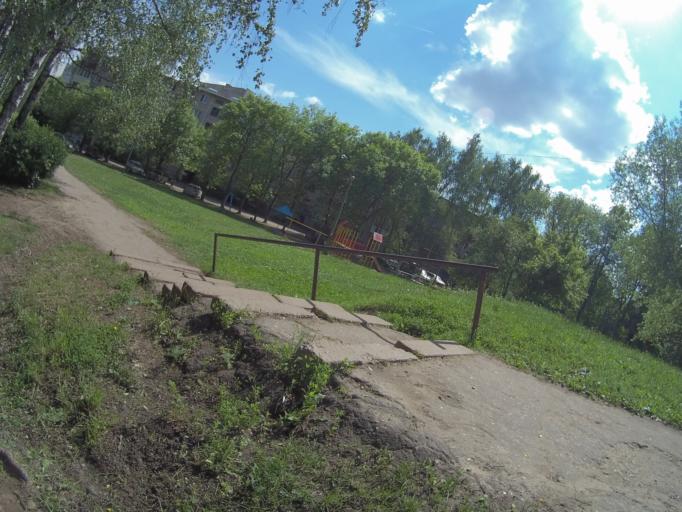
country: RU
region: Vladimir
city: Vladimir
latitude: 56.1281
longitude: 40.3526
